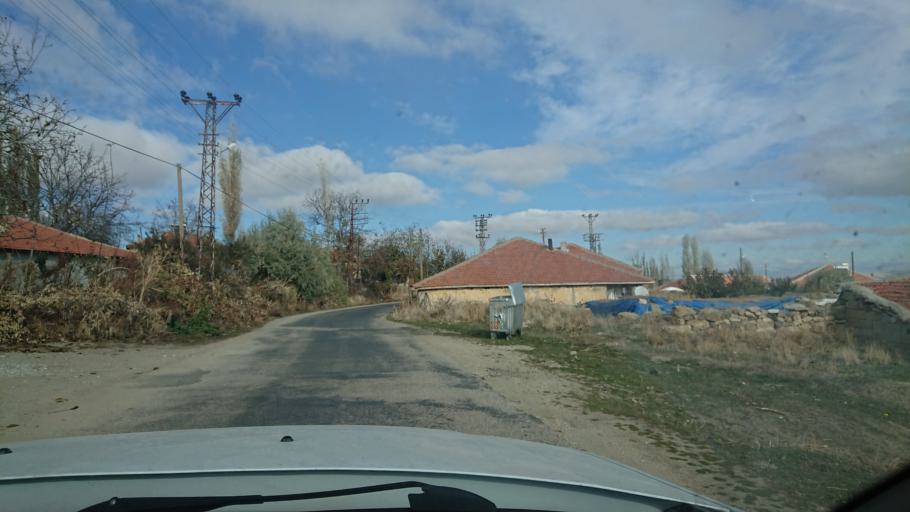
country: TR
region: Aksaray
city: Ortakoy
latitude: 38.8091
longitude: 33.9839
